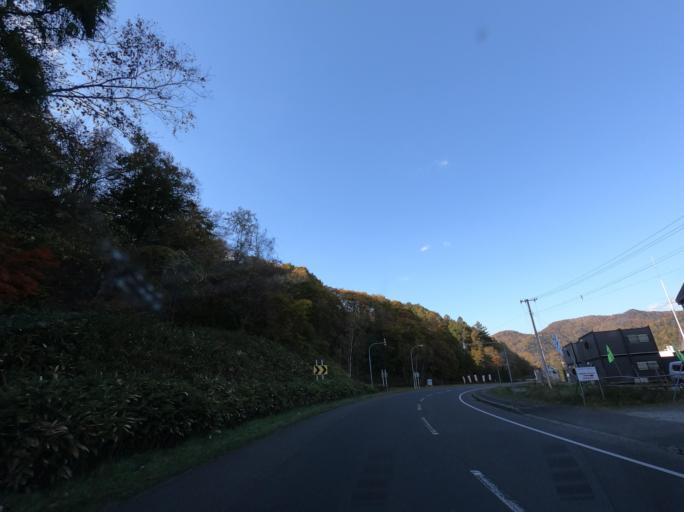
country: JP
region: Hokkaido
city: Iwamizawa
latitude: 43.0001
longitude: 142.0045
